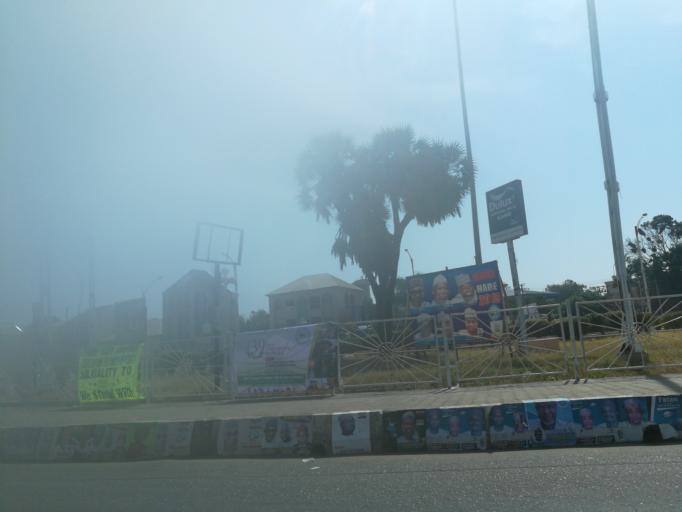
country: NG
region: Kano
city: Kano
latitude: 12.0282
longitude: 8.5151
